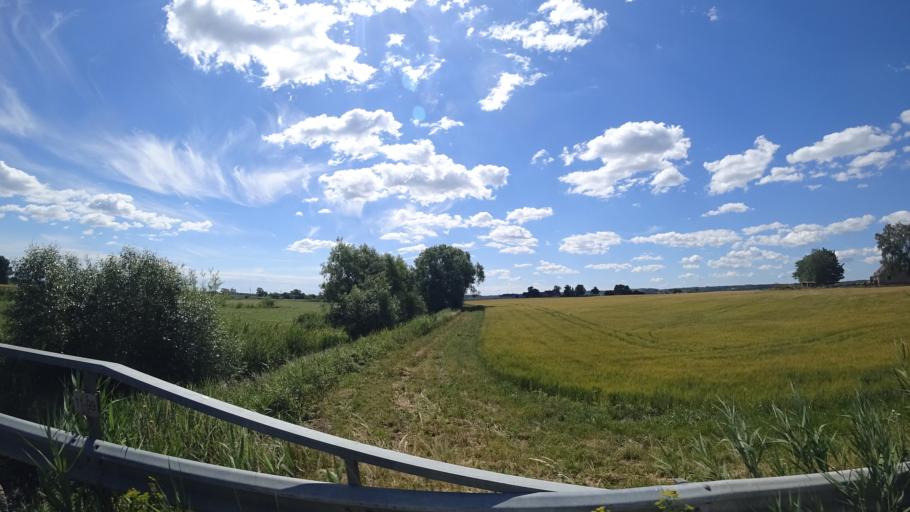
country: SE
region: Skane
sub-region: Kristianstads Kommun
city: Onnestad
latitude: 56.0656
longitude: 14.0503
